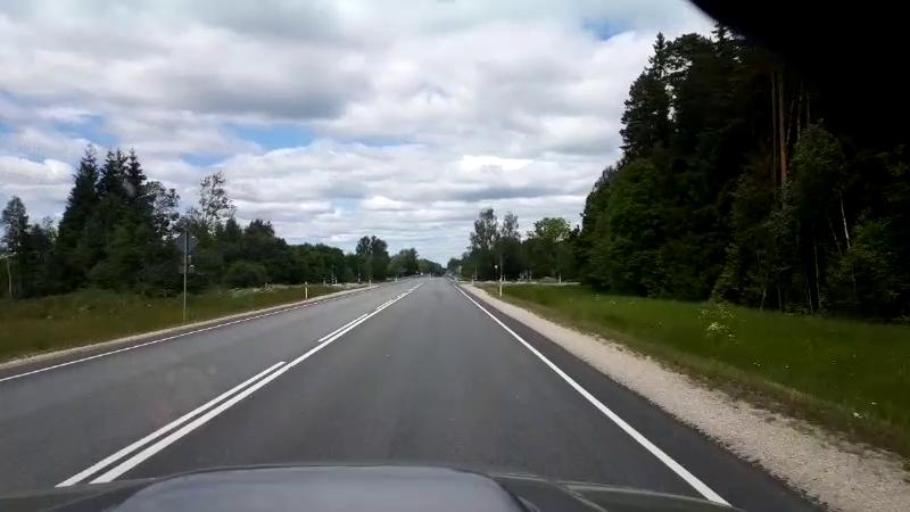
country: EE
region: Raplamaa
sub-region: Maerjamaa vald
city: Marjamaa
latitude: 58.8078
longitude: 24.4126
